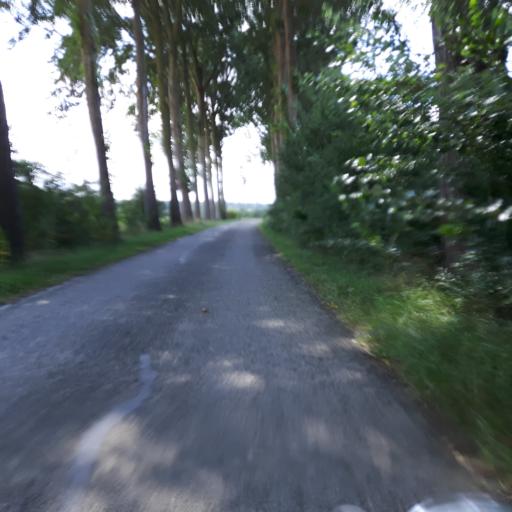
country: NL
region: Zeeland
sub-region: Gemeente Goes
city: Goes
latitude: 51.4594
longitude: 3.8293
